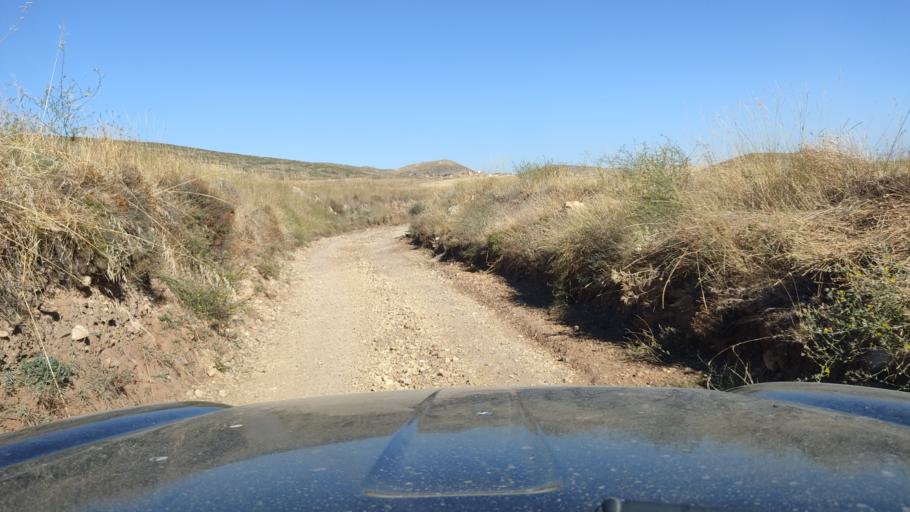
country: ES
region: Aragon
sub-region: Provincia de Teruel
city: Monforte de Moyuela
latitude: 41.0388
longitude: -0.9990
